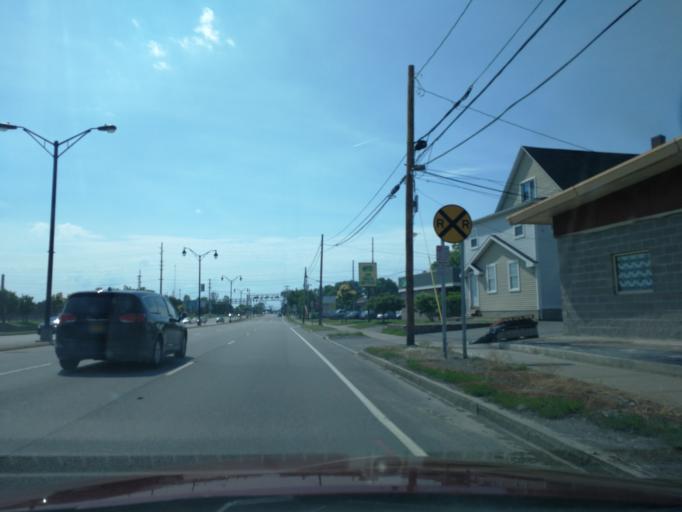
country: US
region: New York
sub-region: Monroe County
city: Greece
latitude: 43.2026
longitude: -77.6450
